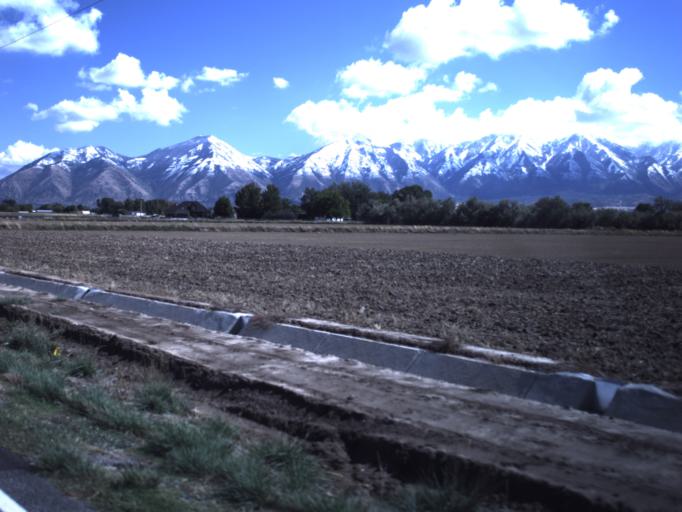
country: US
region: Utah
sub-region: Utah County
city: Benjamin
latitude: 40.0979
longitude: -111.7508
